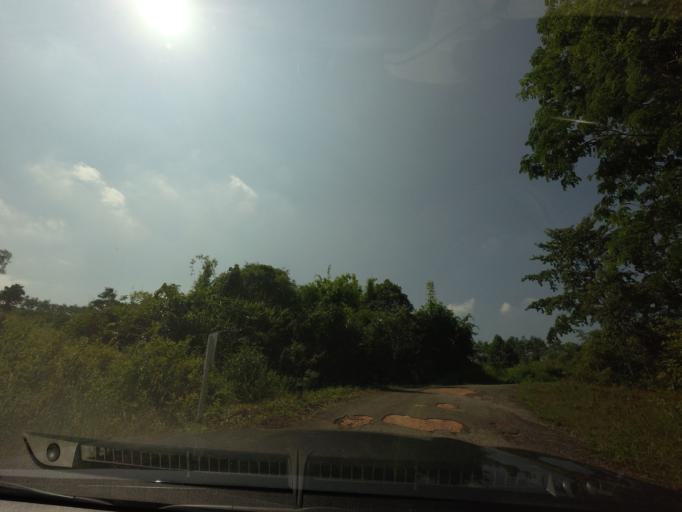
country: TH
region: Loei
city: Na Haeo
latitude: 17.5714
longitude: 100.9585
